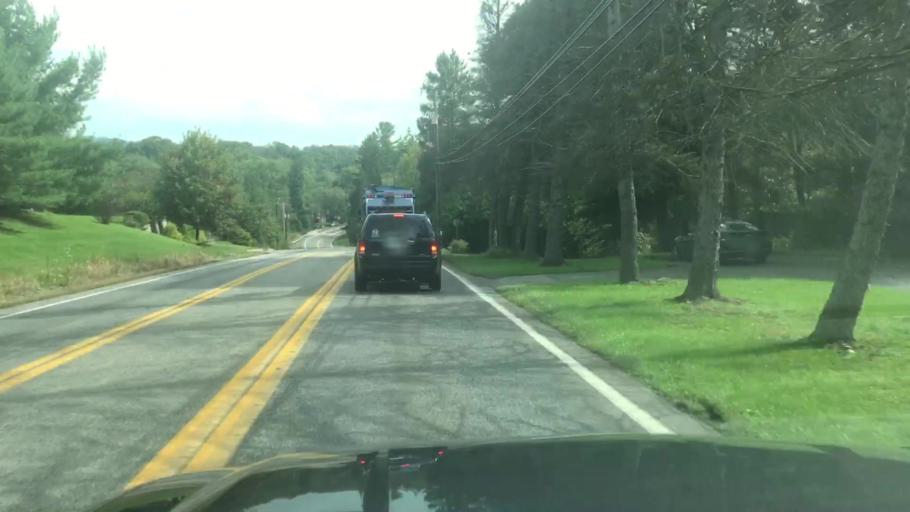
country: US
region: Pennsylvania
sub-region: Cumberland County
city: Shiremanstown
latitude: 40.1850
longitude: -76.9324
